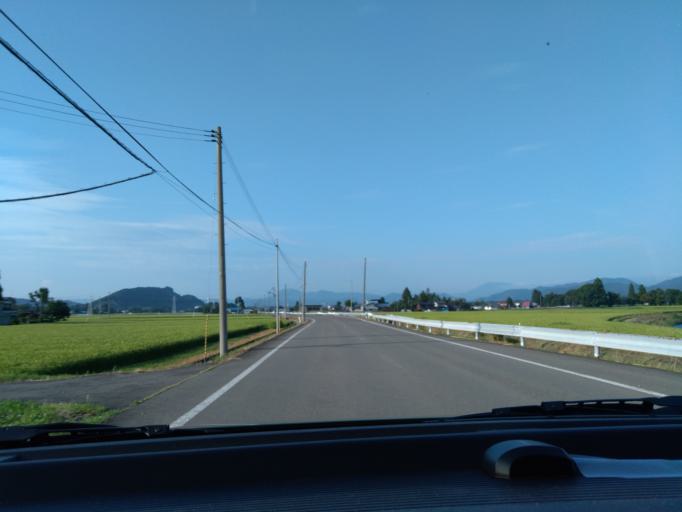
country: JP
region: Akita
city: Kakunodatemachi
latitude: 39.5634
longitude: 140.5769
